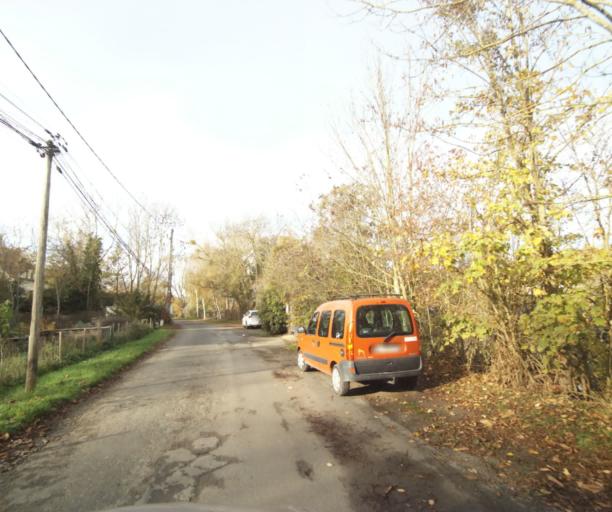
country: FR
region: Ile-de-France
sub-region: Departement du Val-d'Oise
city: Herblay
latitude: 48.9932
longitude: 2.1809
